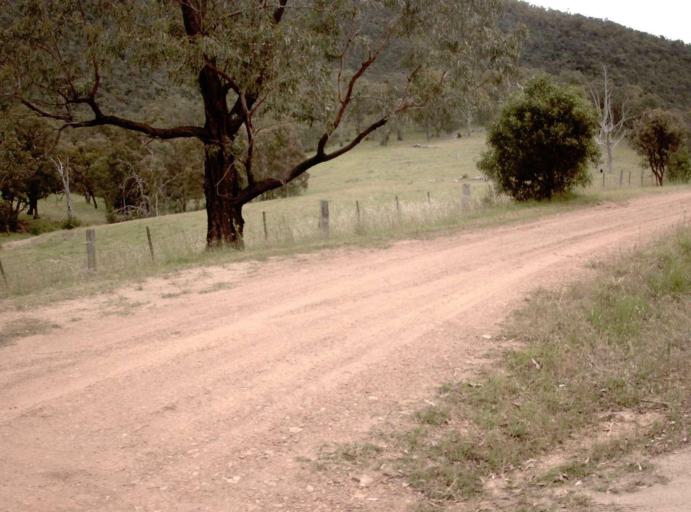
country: AU
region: Victoria
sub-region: East Gippsland
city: Bairnsdale
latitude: -37.5484
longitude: 147.2002
